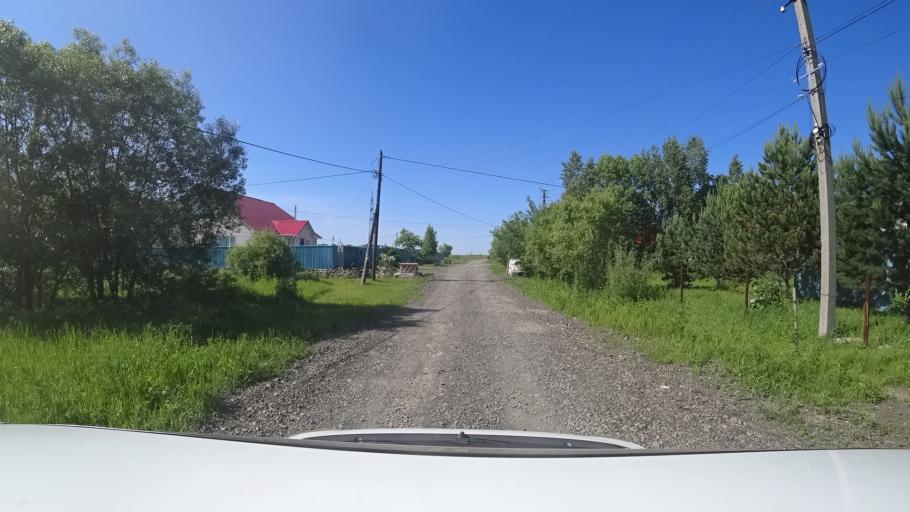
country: RU
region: Khabarovsk Krai
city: Topolevo
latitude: 48.5525
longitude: 135.1691
